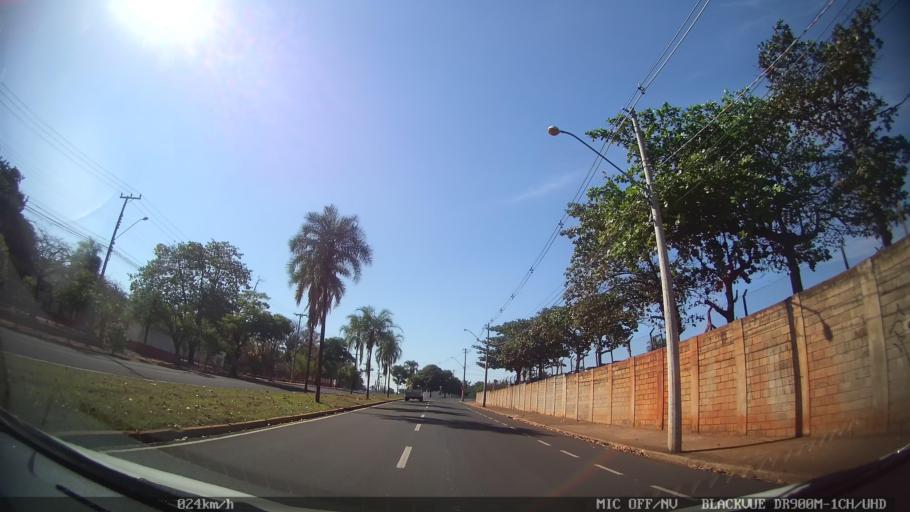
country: BR
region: Sao Paulo
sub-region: Sao Jose Do Rio Preto
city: Sao Jose do Rio Preto
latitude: -20.8107
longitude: -49.4122
